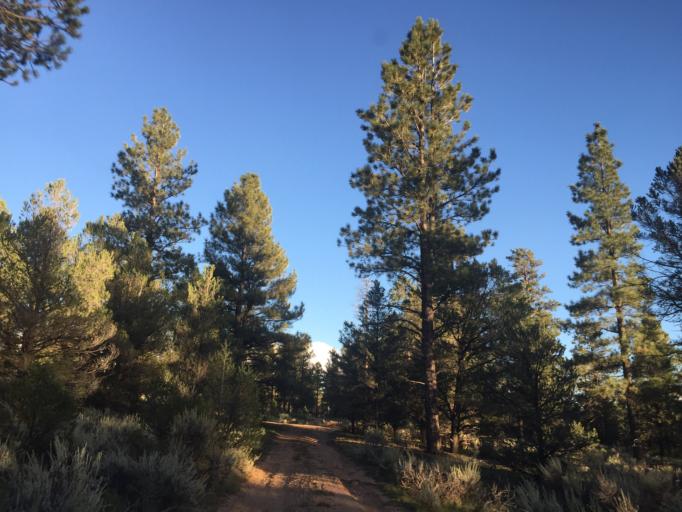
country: US
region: Arizona
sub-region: Coconino County
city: Grand Canyon Village
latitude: 35.9704
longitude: -112.1216
